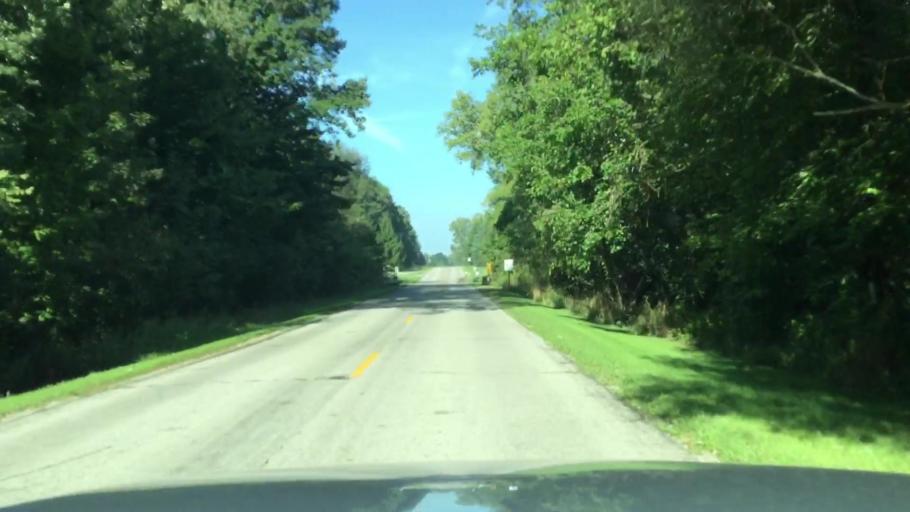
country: US
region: Michigan
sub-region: Lenawee County
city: Manitou Beach-Devils Lake
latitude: 41.9426
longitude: -84.3434
